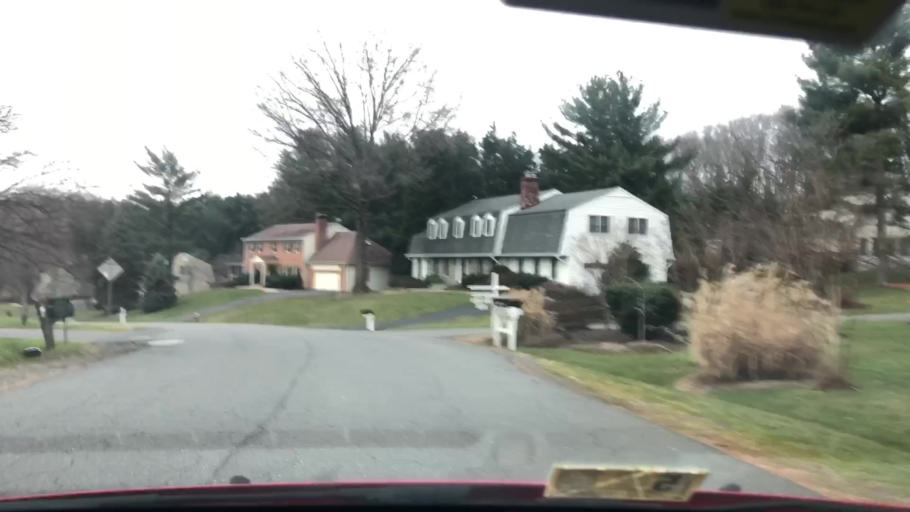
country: US
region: Virginia
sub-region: Fairfax County
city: Wolf Trap
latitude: 38.9636
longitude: -77.2724
